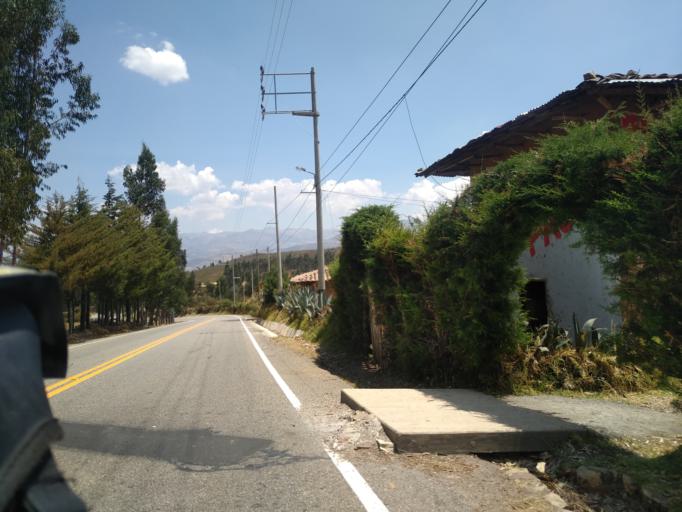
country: PE
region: Cajamarca
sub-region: San Marcos
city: San Marcos
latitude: -7.2920
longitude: -78.2053
